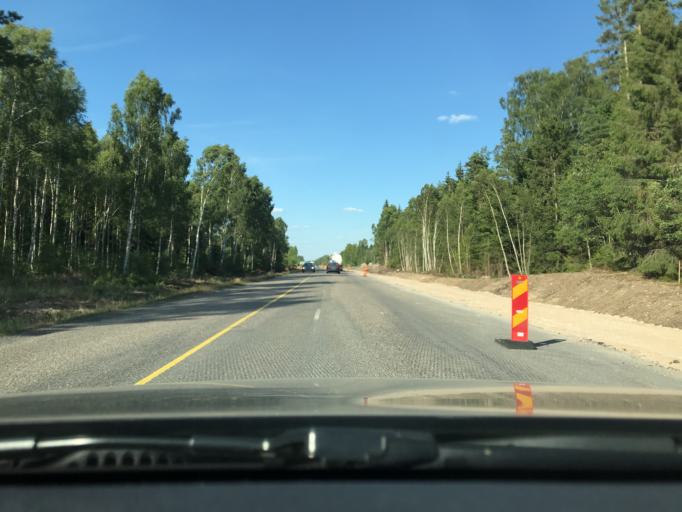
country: SE
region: Kronoberg
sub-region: Almhults Kommun
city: AElmhult
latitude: 56.5532
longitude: 14.1712
